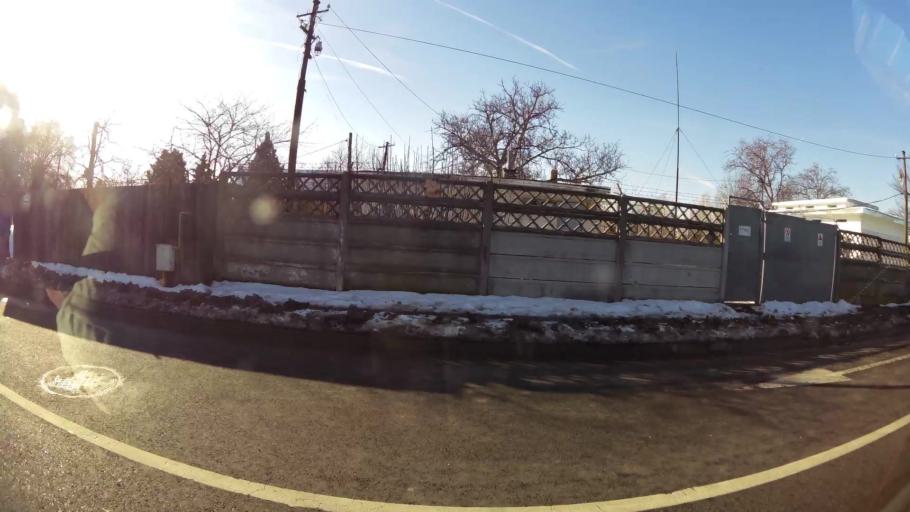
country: RO
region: Ilfov
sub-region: Comuna Fundeni-Dobroesti
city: Fundeni
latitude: 44.4726
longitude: 26.1413
